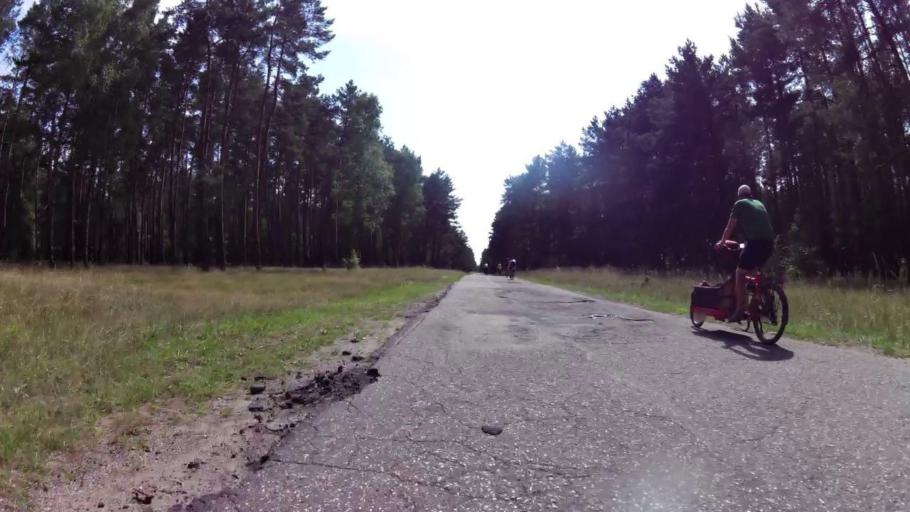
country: PL
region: West Pomeranian Voivodeship
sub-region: Powiat choszczenski
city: Drawno
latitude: 53.3279
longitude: 15.6932
